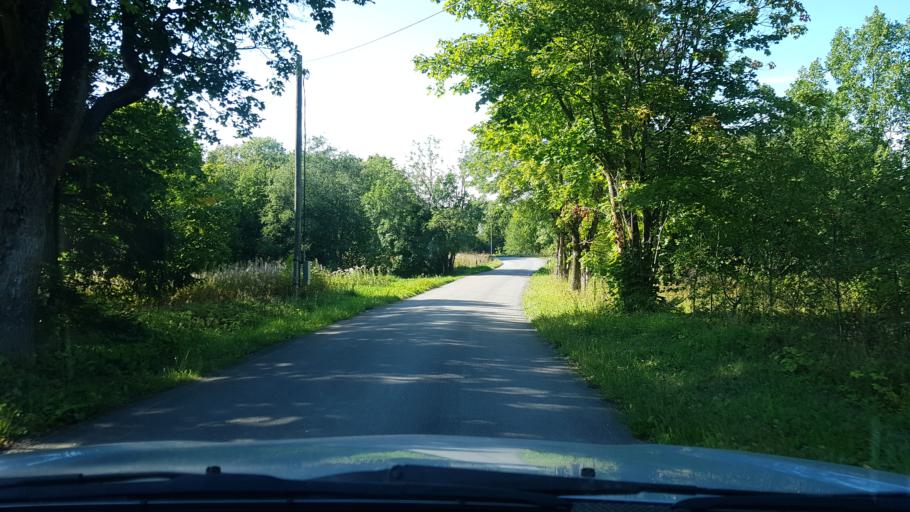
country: EE
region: Ida-Virumaa
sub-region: Narva-Joesuu linn
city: Narva-Joesuu
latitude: 59.4076
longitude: 27.9901
